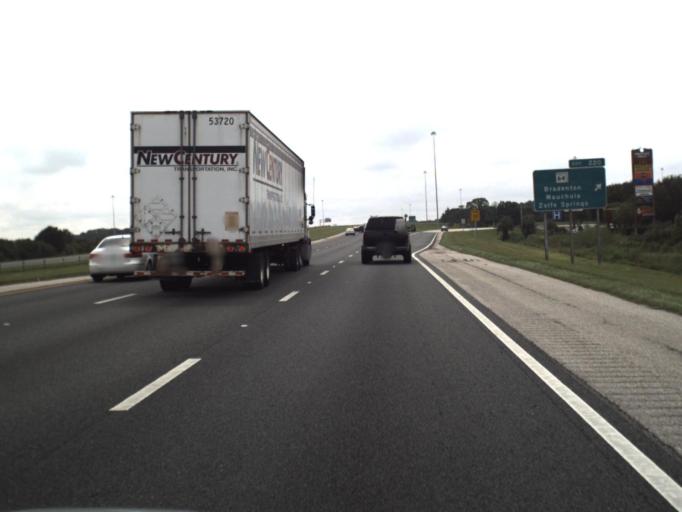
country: US
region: Florida
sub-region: Manatee County
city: Ellenton
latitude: 27.4968
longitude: -82.4751
